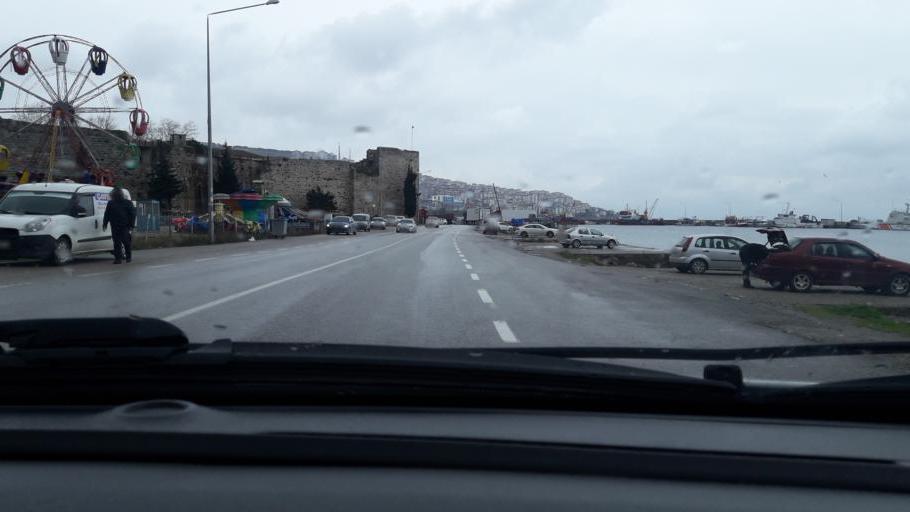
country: TR
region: Sinop
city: Sinop
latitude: 42.0238
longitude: 35.1413
